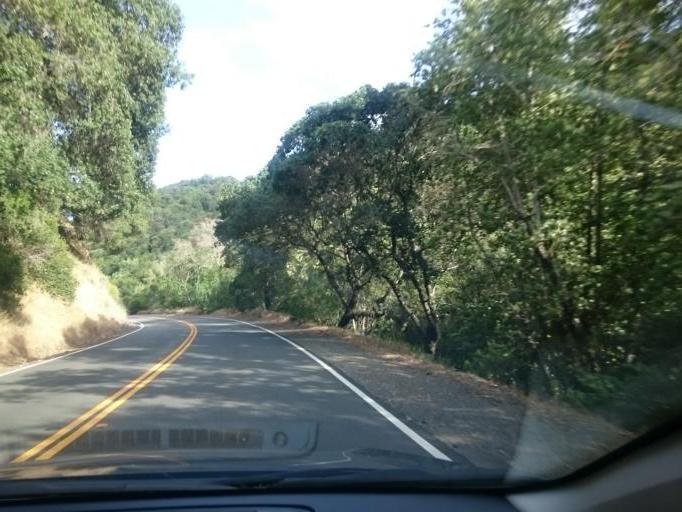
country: US
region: California
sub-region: Napa County
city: Yountville
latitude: 38.4885
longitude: -122.3197
